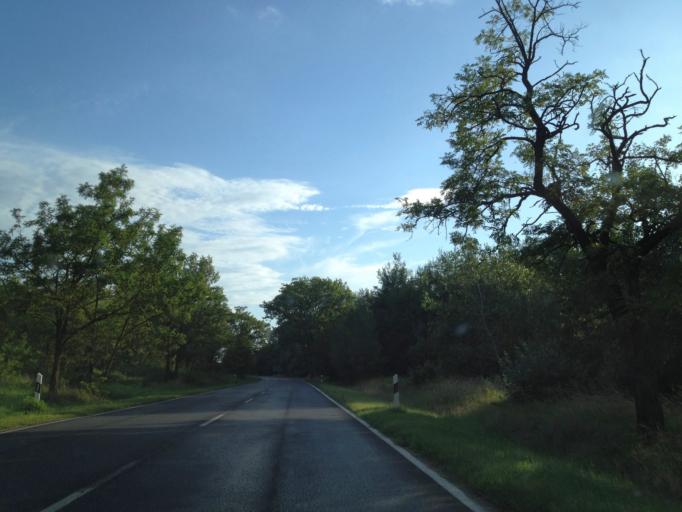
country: HU
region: Gyor-Moson-Sopron
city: Gyor
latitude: 47.7179
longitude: 17.6856
